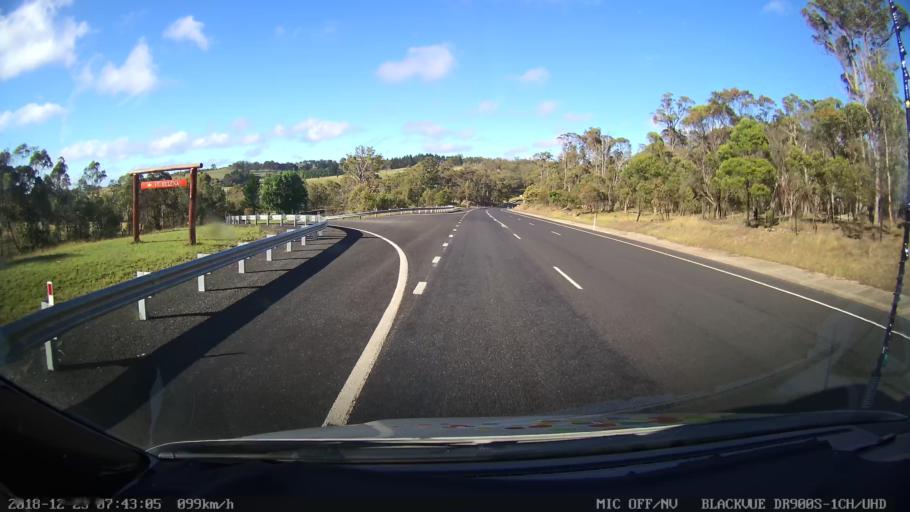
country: AU
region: New South Wales
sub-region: Armidale Dumaresq
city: Enmore
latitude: -30.5196
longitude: 151.9694
